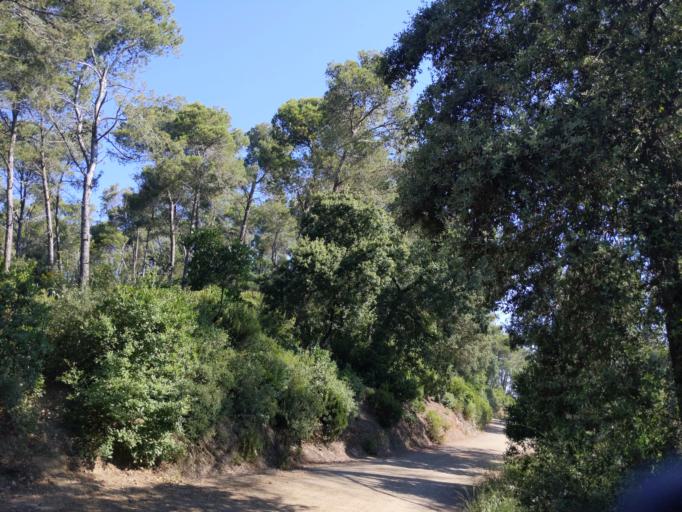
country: ES
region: Catalonia
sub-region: Provincia de Barcelona
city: Cerdanyola del Valles
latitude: 41.4551
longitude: 2.1370
